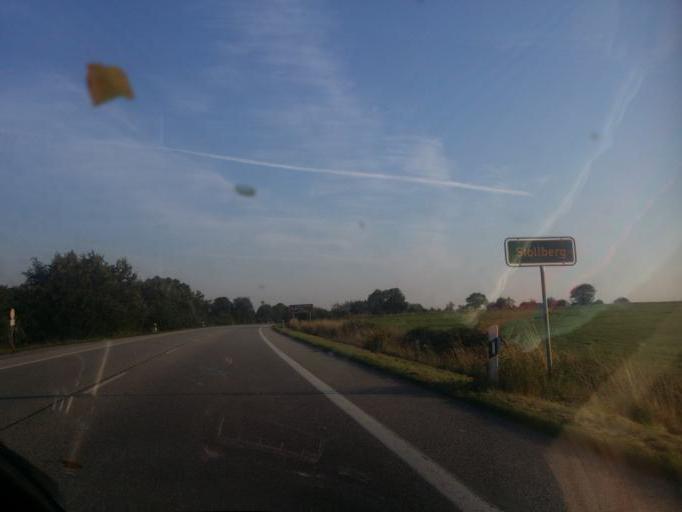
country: DE
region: Schleswig-Holstein
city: Bordelum
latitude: 54.6426
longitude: 8.9470
